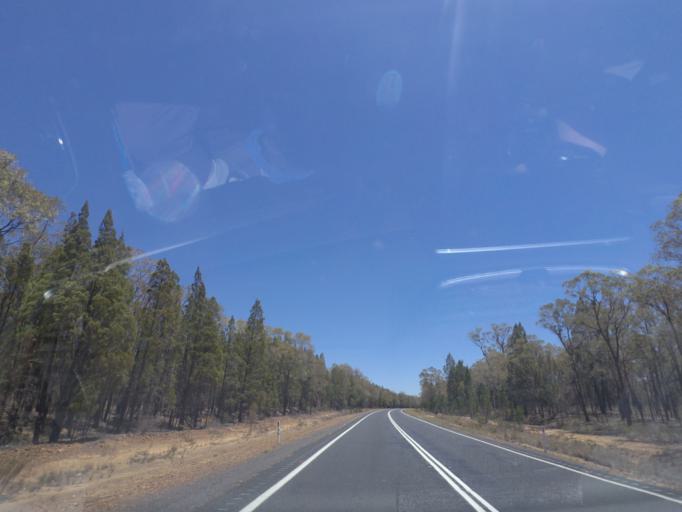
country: AU
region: New South Wales
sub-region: Warrumbungle Shire
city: Coonabarabran
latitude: -31.1970
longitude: 149.3495
